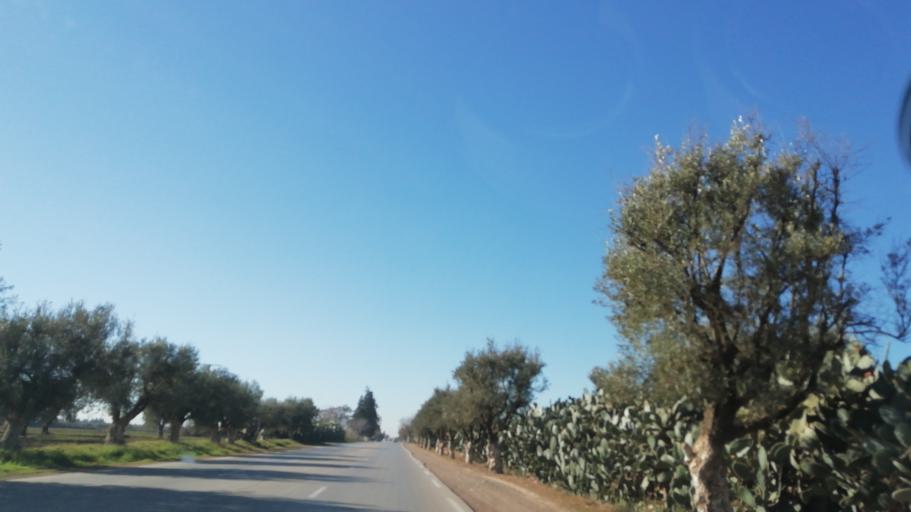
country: MA
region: Oriental
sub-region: Oujda-Angad
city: Oujda
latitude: 34.8247
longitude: -1.7965
